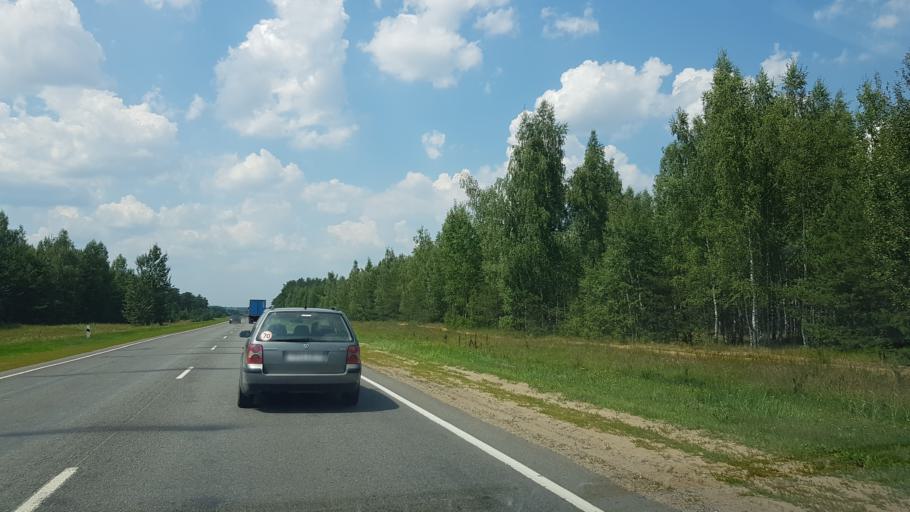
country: BY
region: Mogilev
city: Babruysk
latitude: 53.1633
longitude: 29.3016
